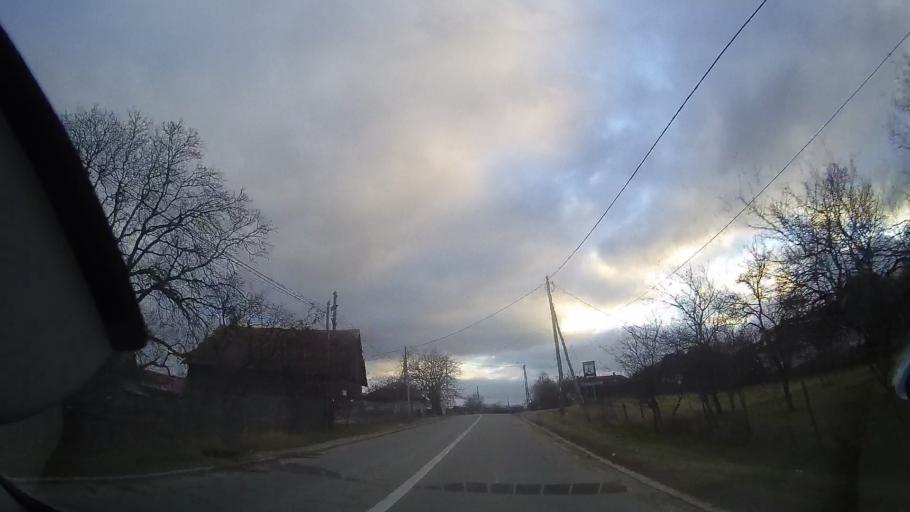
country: RO
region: Cluj
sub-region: Comuna Sancraiu
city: Sancraiu
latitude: 46.8044
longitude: 22.9946
